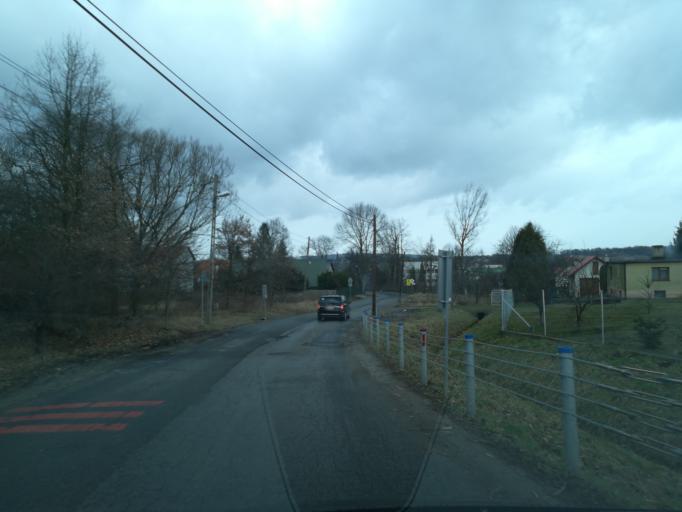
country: PL
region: Lesser Poland Voivodeship
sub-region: Krakow
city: Sidzina
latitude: 49.9857
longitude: 19.8731
